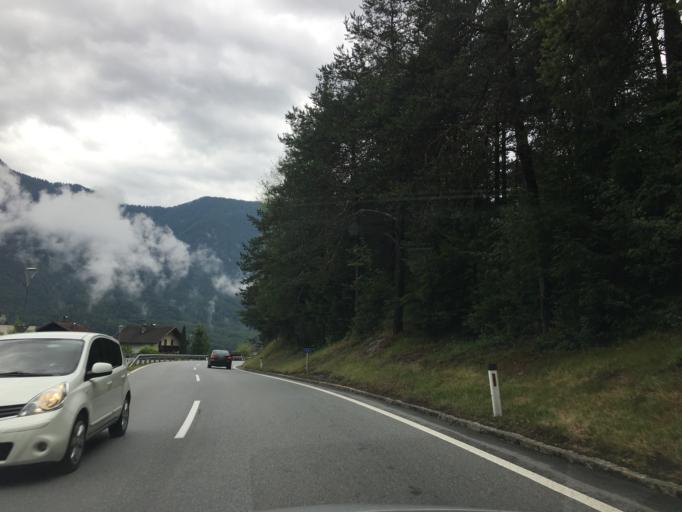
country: AT
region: Tyrol
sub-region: Politischer Bezirk Imst
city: Nassereith
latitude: 47.3012
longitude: 10.8349
